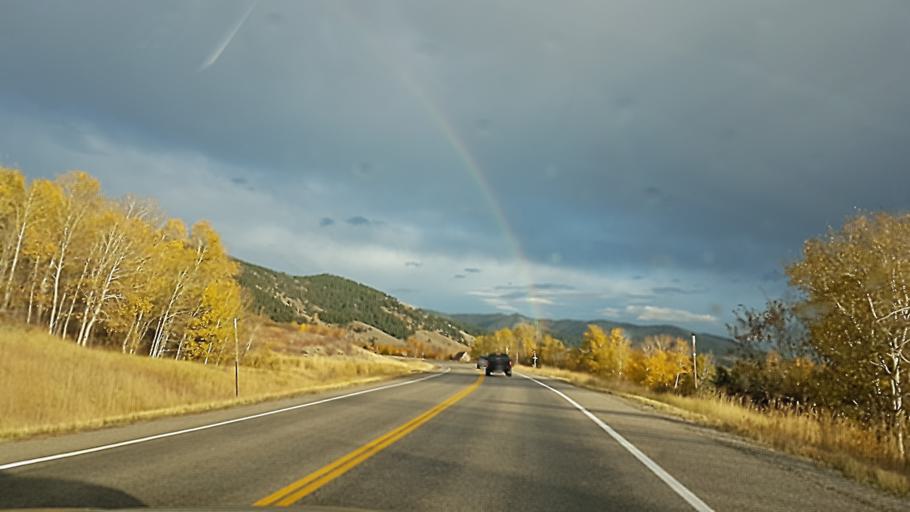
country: US
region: Montana
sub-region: Gallatin County
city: West Yellowstone
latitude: 44.6635
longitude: -111.3825
